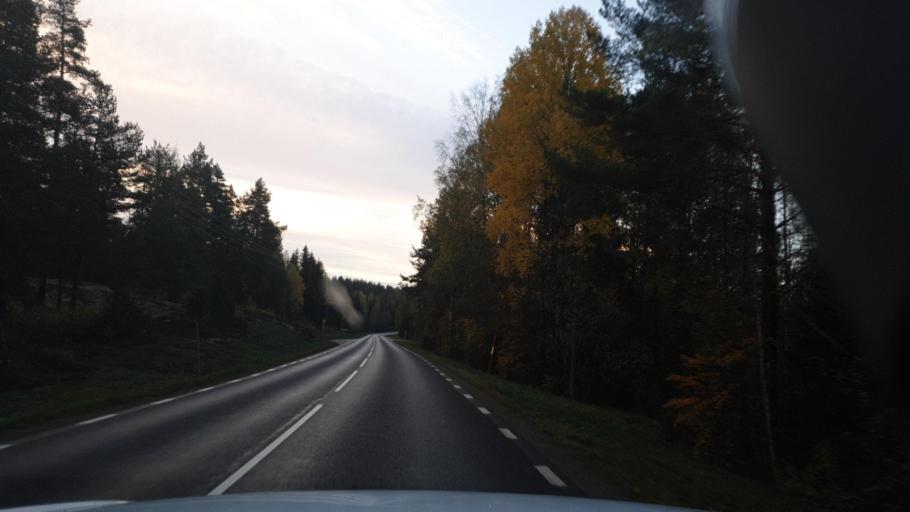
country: SE
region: Vaermland
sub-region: Arvika Kommun
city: Arvika
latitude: 59.7328
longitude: 12.5618
